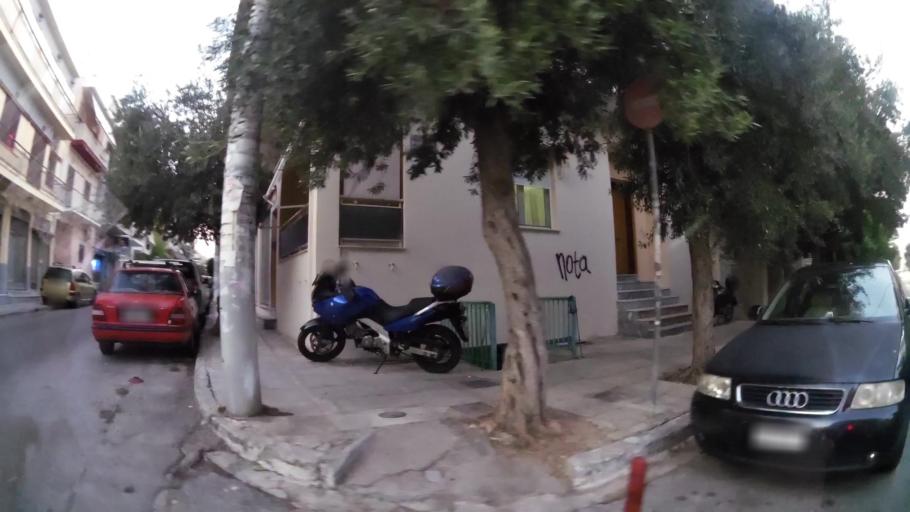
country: GR
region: Attica
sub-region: Nomos Piraios
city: Nikaia
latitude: 37.9735
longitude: 23.6478
